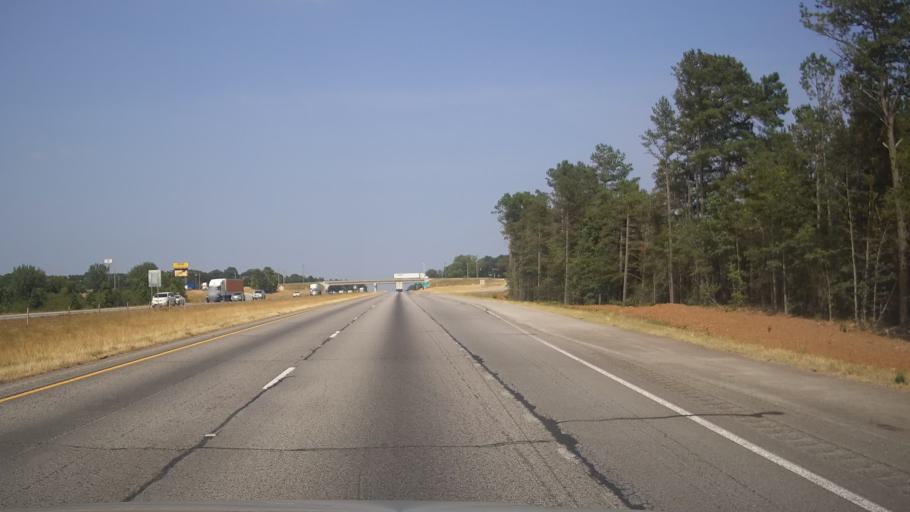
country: US
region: Georgia
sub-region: Franklin County
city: Carnesville
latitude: 34.3889
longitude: -83.2336
